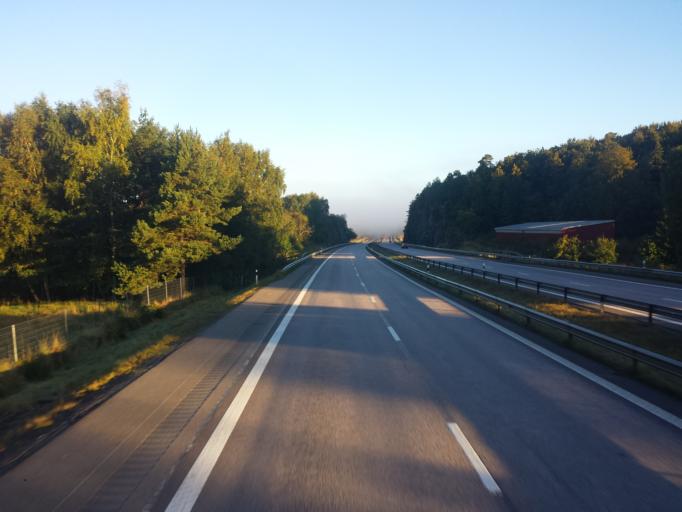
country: SE
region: Halland
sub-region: Kungsbacka Kommun
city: Fjaeras kyrkby
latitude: 57.4111
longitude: 12.1725
